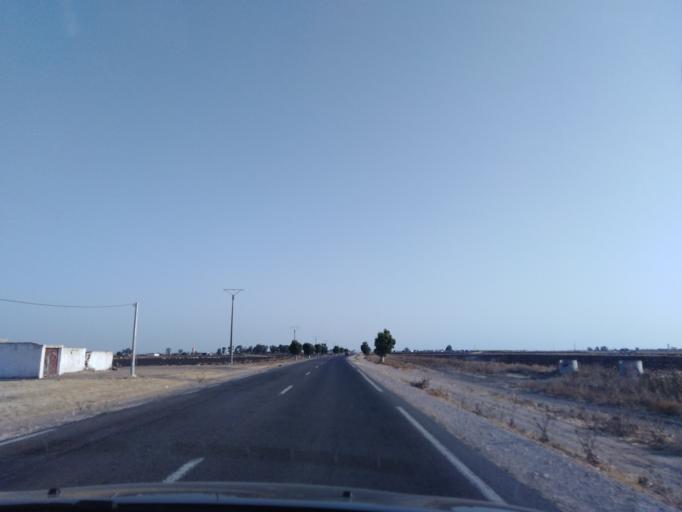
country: MA
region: Doukkala-Abda
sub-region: Safi
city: Youssoufia
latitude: 32.4787
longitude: -8.7700
